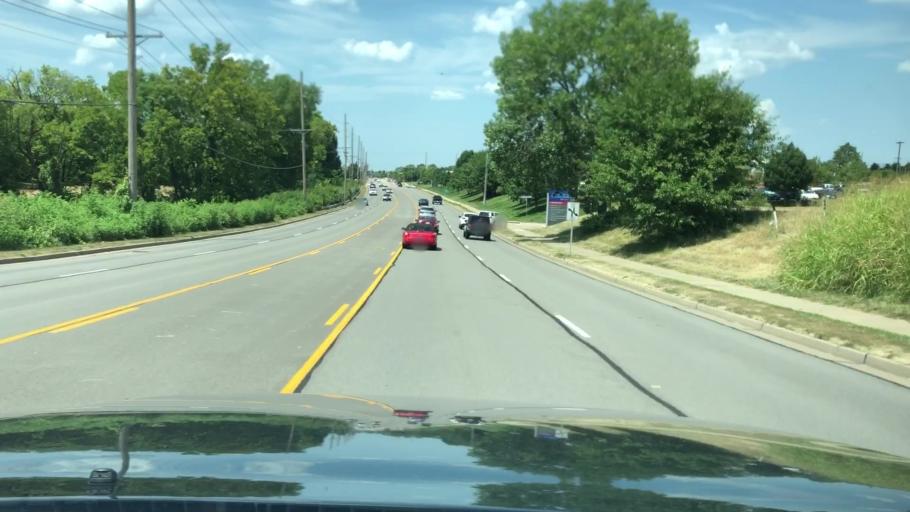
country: US
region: Missouri
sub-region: Saint Charles County
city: Saint Peters
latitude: 38.7918
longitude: -90.5785
